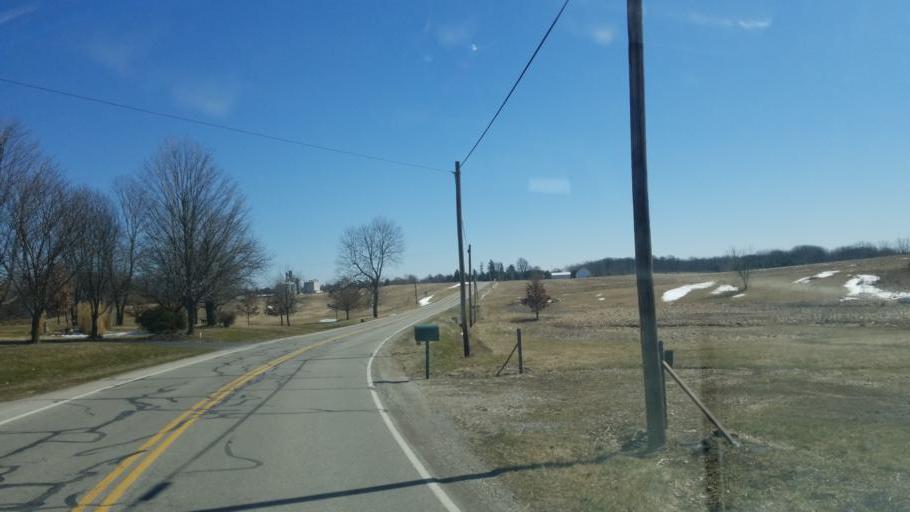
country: US
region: Ohio
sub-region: Crawford County
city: Bucyrus
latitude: 40.8070
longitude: -83.0046
